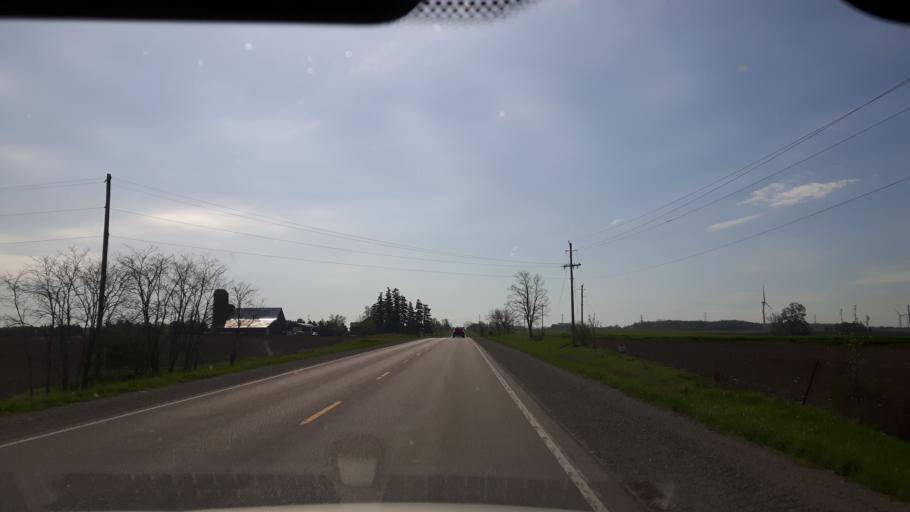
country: CA
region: Ontario
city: Bluewater
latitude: 43.5496
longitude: -81.6618
